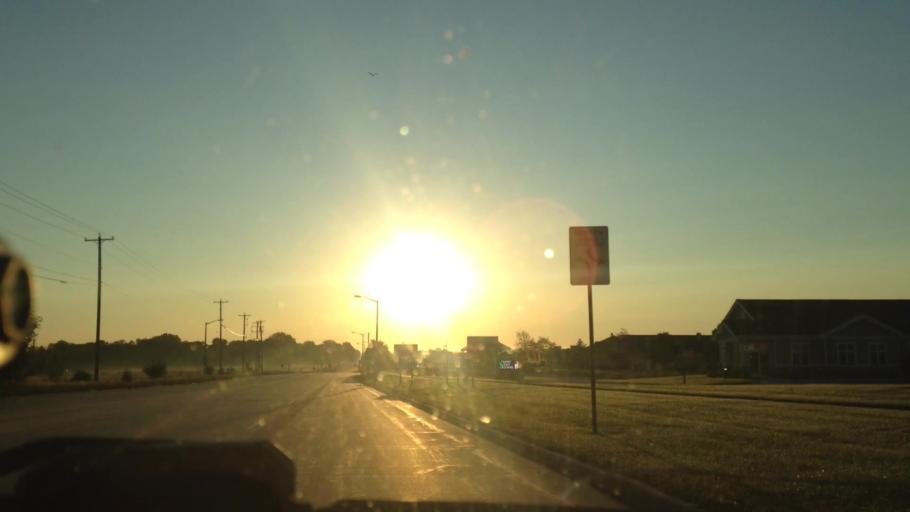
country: US
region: Wisconsin
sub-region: Washington County
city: West Bend
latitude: 43.4266
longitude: -88.1451
